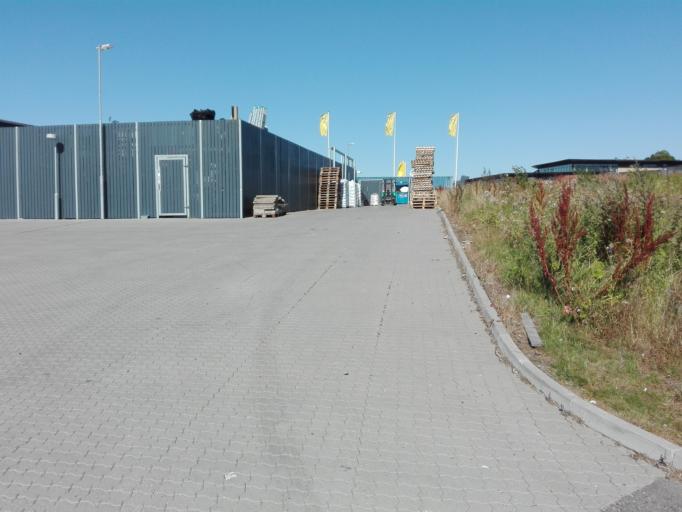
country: DK
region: Central Jutland
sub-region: Arhus Kommune
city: Tranbjerg
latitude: 56.1028
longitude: 10.1450
